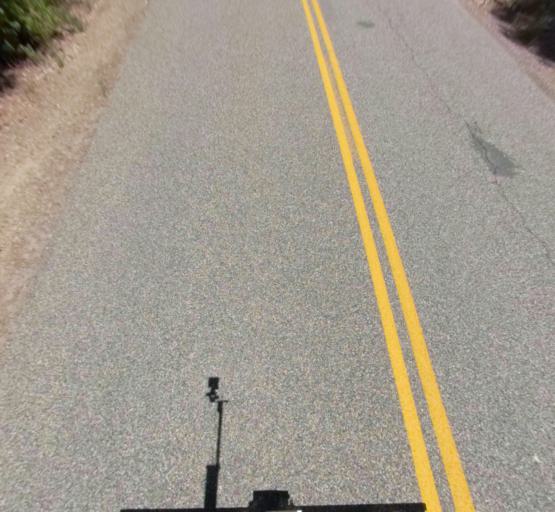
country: US
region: California
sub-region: Madera County
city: Oakhurst
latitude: 37.3421
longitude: -119.5531
